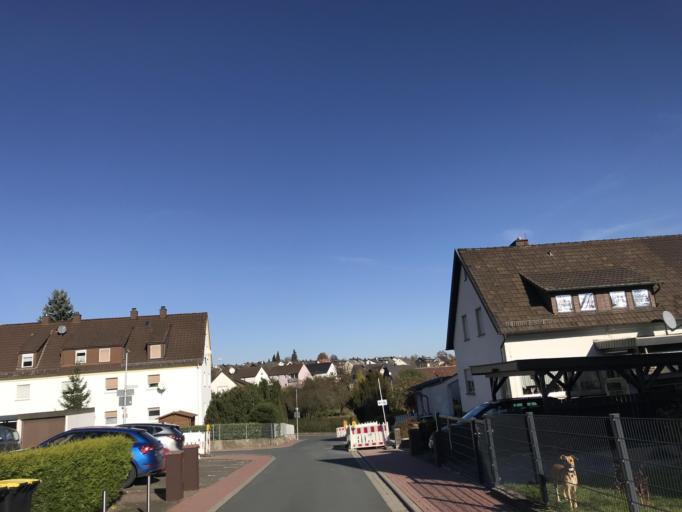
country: DE
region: Hesse
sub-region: Regierungsbezirk Giessen
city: Braunfels
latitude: 50.5116
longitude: 8.3969
